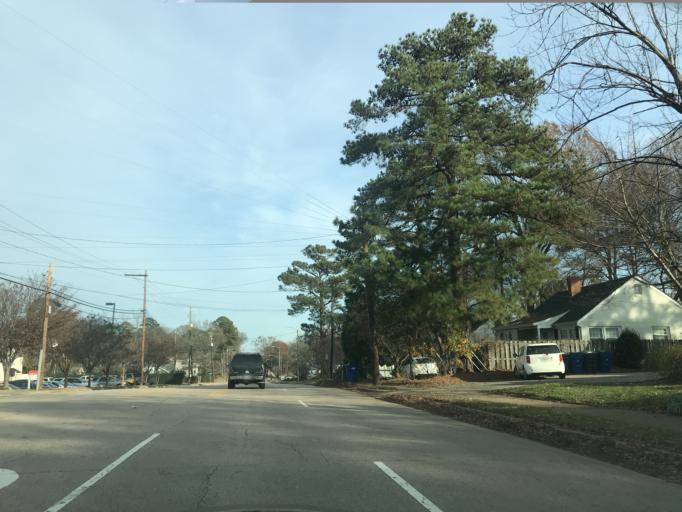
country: US
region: North Carolina
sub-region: Wake County
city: Raleigh
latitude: 35.8067
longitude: -78.6313
